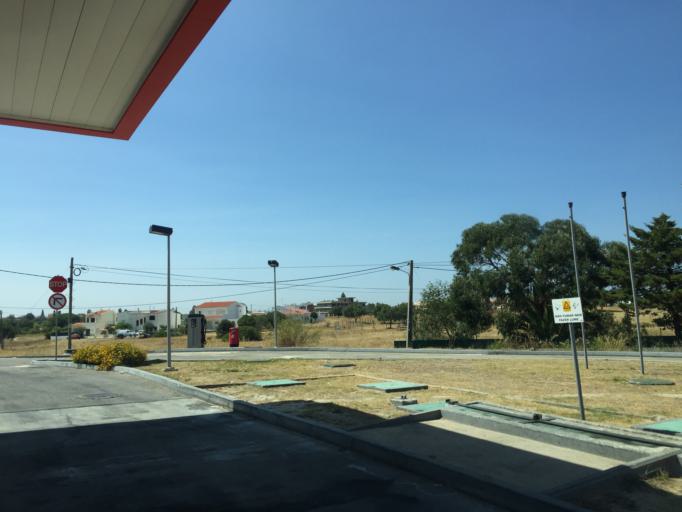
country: PT
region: Faro
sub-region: Albufeira
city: Ferreiras
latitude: 37.1235
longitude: -8.2321
